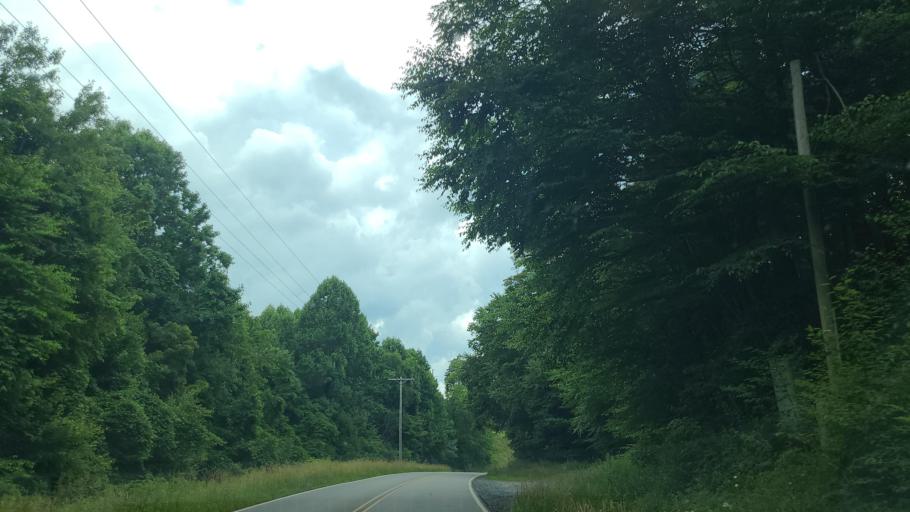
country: US
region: North Carolina
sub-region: Ashe County
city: Jefferson
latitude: 36.3931
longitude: -81.3445
